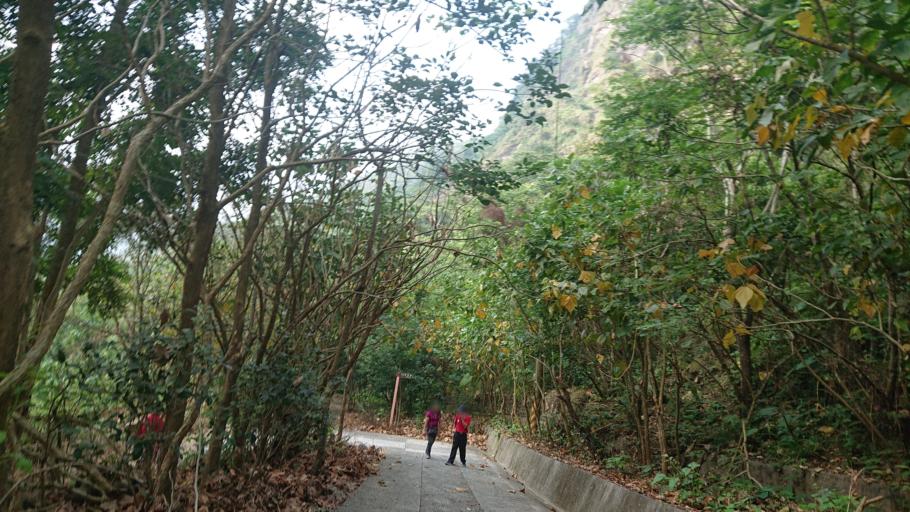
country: TW
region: Taiwan
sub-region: Yunlin
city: Douliu
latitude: 23.6023
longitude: 120.6679
